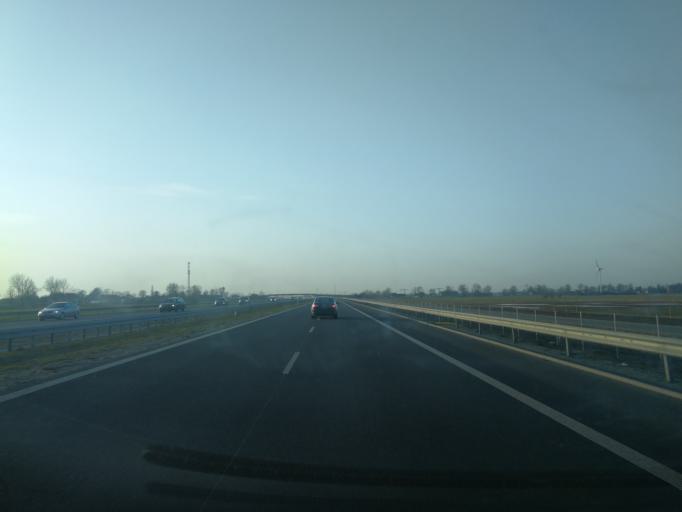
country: PL
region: Pomeranian Voivodeship
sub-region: Powiat nowodworski
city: Ostaszewo
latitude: 54.2469
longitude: 18.9934
